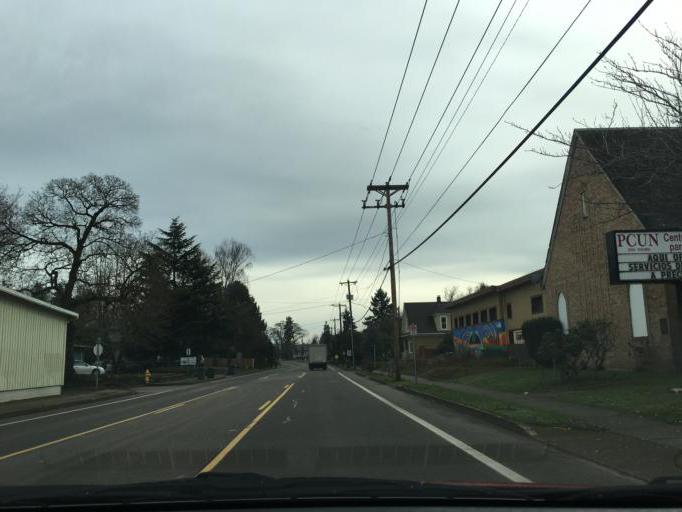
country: US
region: Oregon
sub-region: Marion County
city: Woodburn
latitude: 45.1412
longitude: -122.8549
